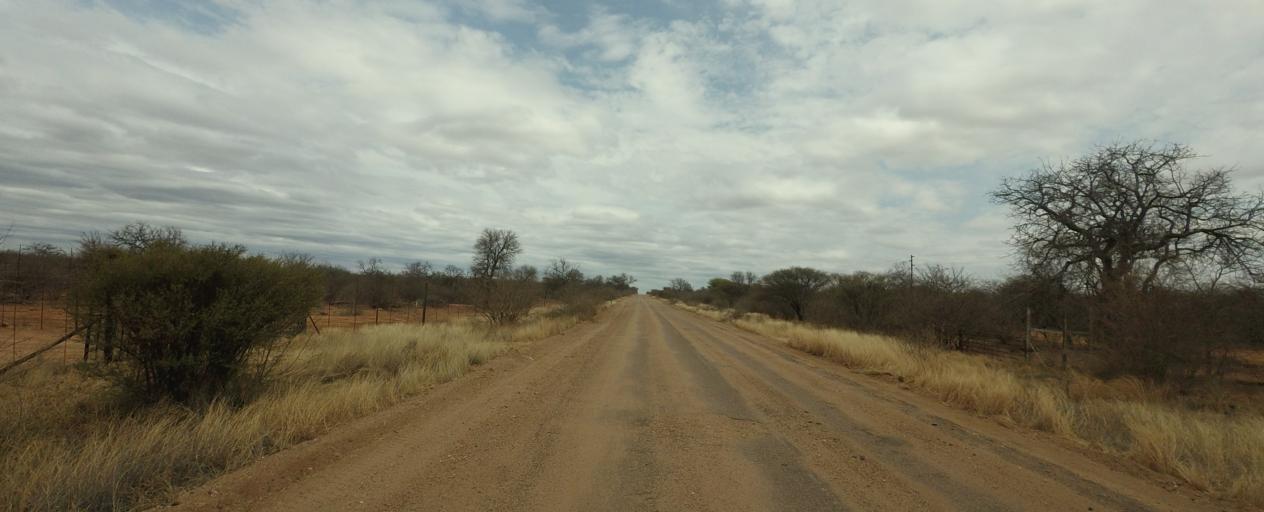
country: BW
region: Central
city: Mathathane
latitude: -22.6698
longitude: 28.6857
